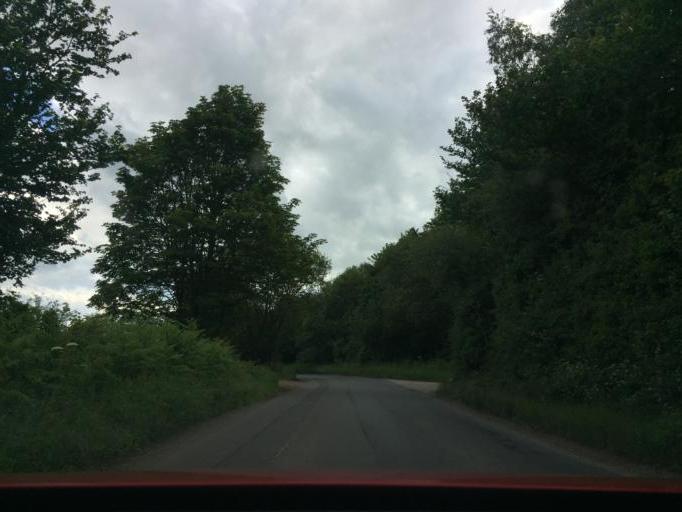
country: GB
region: England
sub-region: Hertfordshire
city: Harpenden
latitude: 51.8563
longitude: -0.3588
